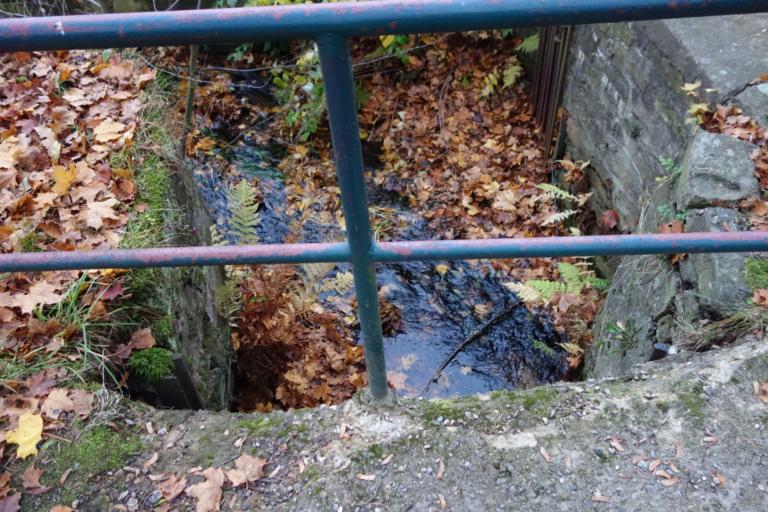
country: DE
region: Saxony
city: Olbernhau
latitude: 50.6487
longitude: 13.3688
